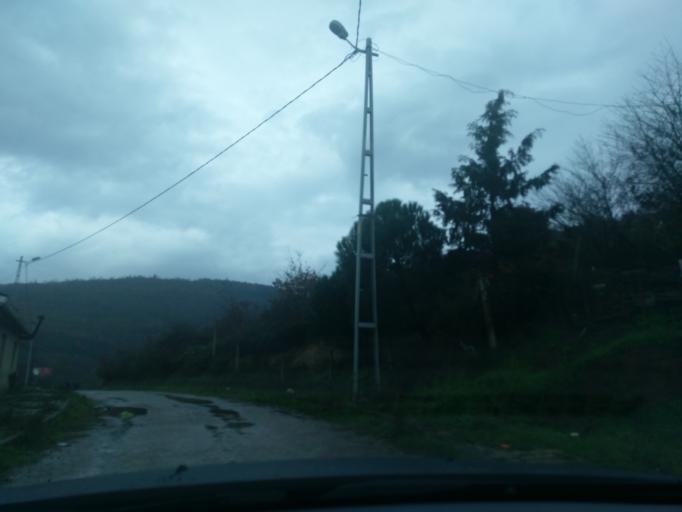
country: TR
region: Istanbul
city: Sancaktepe
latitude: 41.0265
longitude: 29.2496
